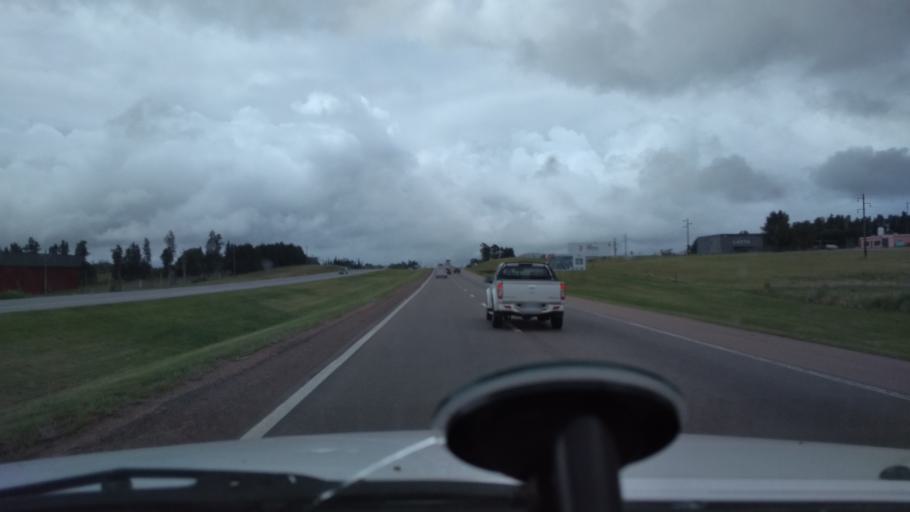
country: UY
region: Canelones
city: Las Piedras
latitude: -34.7357
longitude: -56.2499
